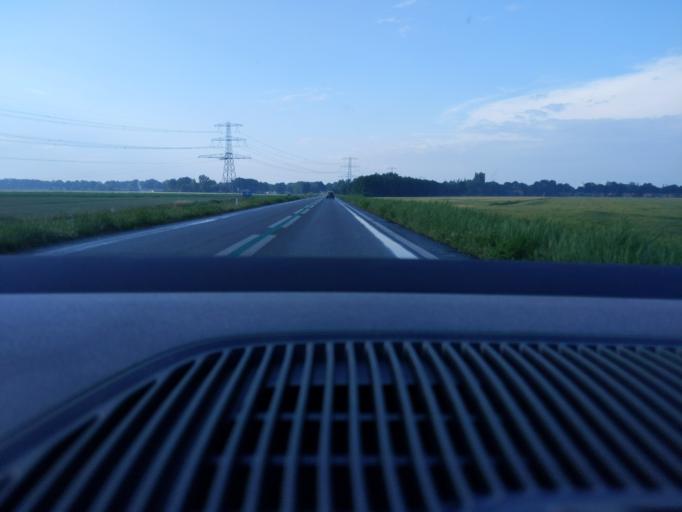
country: NL
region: Drenthe
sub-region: Gemeente Emmen
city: Emmer-Compascuum
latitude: 52.9094
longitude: 7.0380
